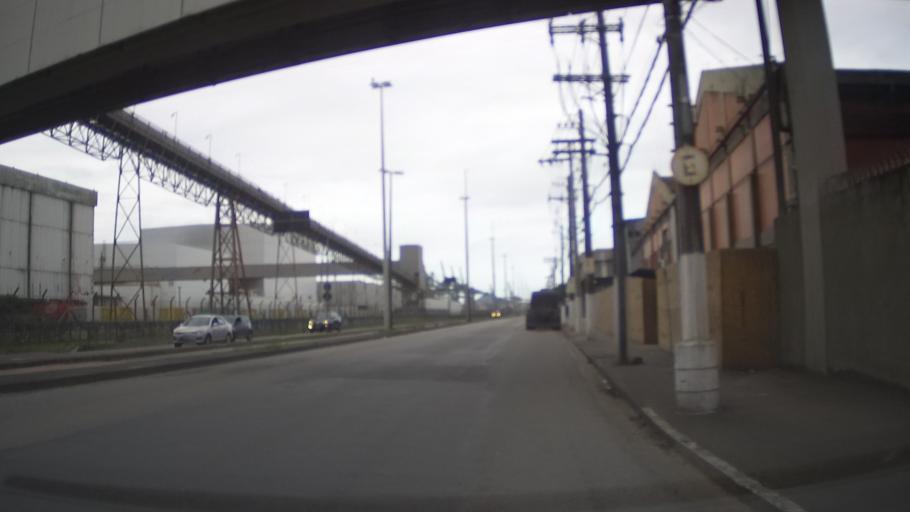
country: BR
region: Sao Paulo
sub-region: Santos
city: Santos
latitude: -23.9613
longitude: -46.3062
